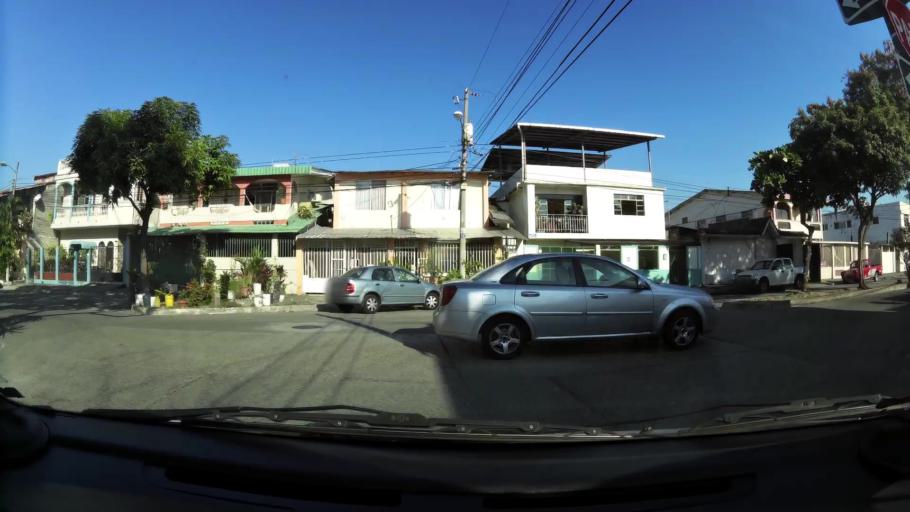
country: EC
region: Guayas
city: Eloy Alfaro
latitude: -2.1679
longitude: -79.8870
